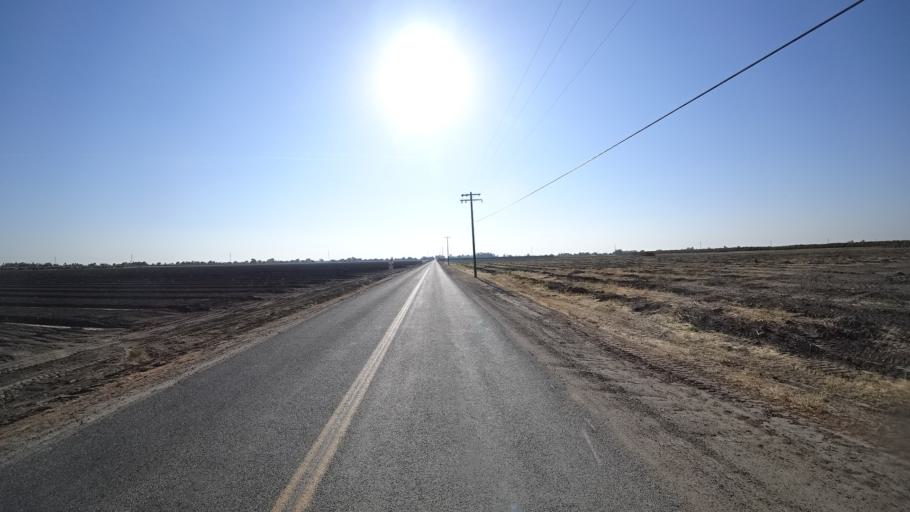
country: US
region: California
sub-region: Fresno County
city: Riverdale
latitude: 36.3765
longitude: -119.9047
